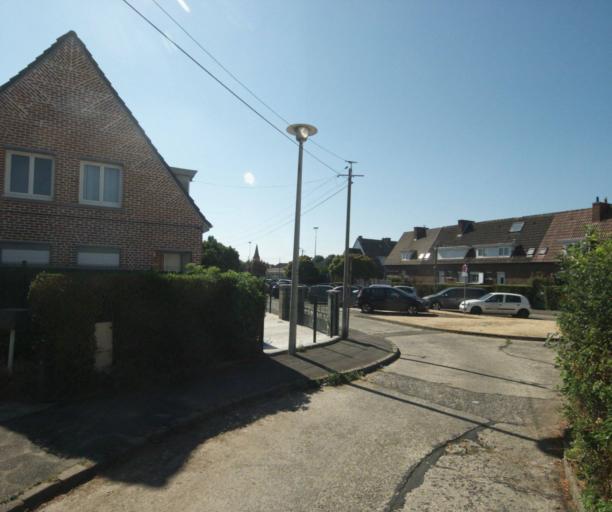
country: FR
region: Nord-Pas-de-Calais
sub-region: Departement du Nord
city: Wattrelos
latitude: 50.7022
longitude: 3.2018
